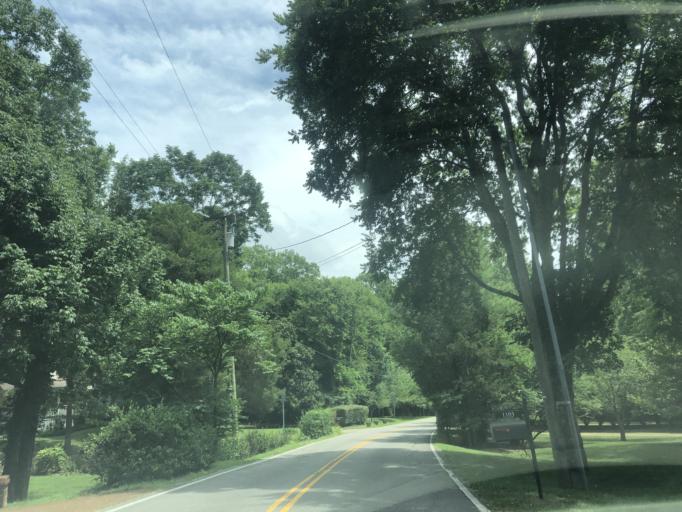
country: US
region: Tennessee
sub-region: Davidson County
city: Forest Hills
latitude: 36.0651
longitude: -86.8117
